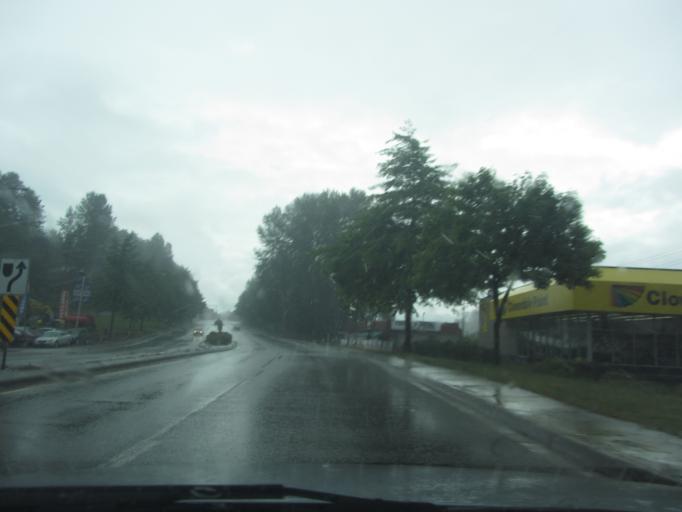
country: CA
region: British Columbia
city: Abbotsford
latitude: 49.1330
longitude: -122.3162
